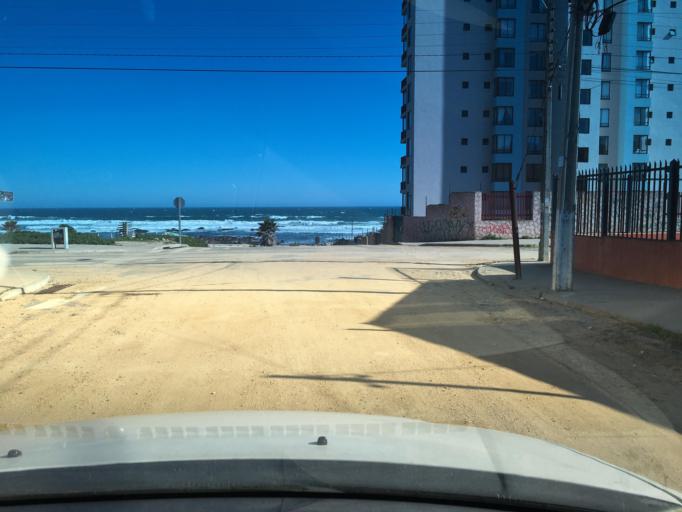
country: CL
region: Valparaiso
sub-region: San Antonio Province
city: El Tabo
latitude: -33.4583
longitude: -71.6614
